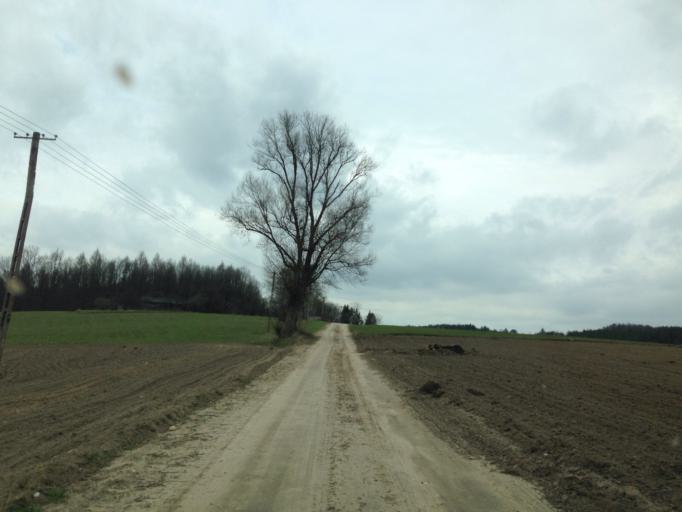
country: PL
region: Warmian-Masurian Voivodeship
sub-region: Powiat dzialdowski
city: Lidzbark
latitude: 53.2133
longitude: 19.7453
